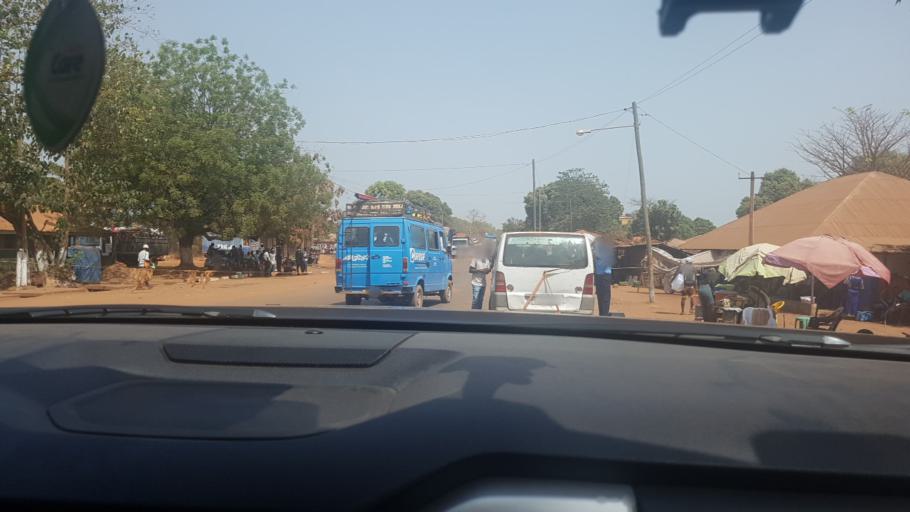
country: GW
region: Bissau
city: Bissau
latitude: 11.9436
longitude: -15.6466
